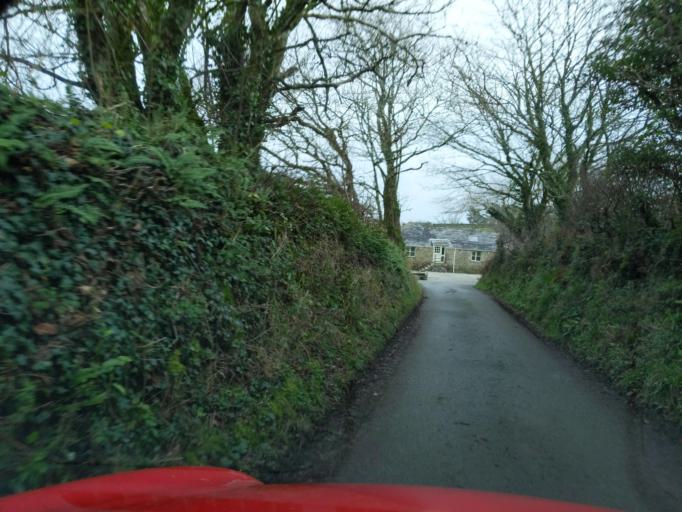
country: GB
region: England
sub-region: Cornwall
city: Duloe
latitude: 50.3526
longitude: -4.5131
